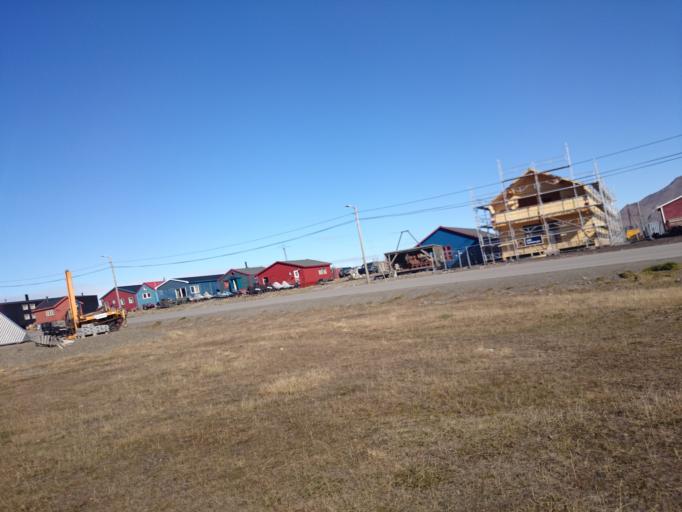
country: SJ
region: Svalbard
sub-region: Spitsbergen
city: Longyearbyen
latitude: 78.2227
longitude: 15.6586
